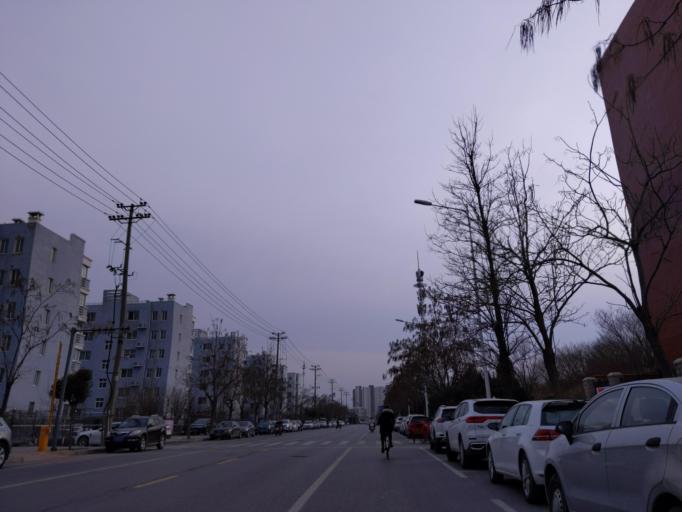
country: CN
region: Henan Sheng
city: Zhongyuanlu
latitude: 35.7593
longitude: 115.0407
